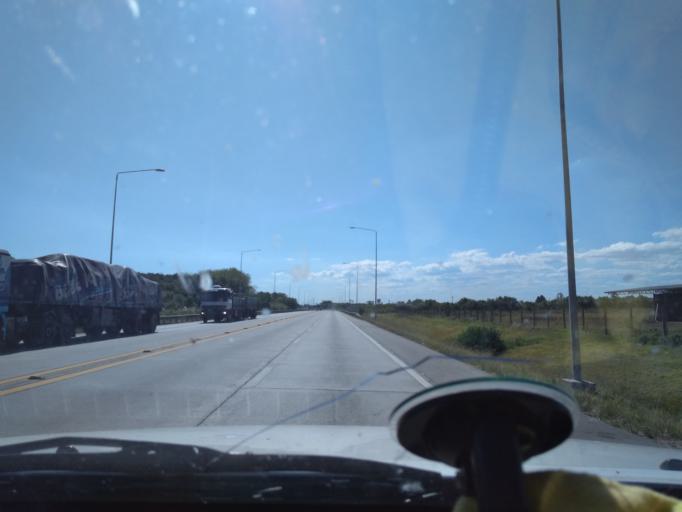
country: UY
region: Canelones
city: La Paz
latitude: -34.7814
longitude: -56.2549
